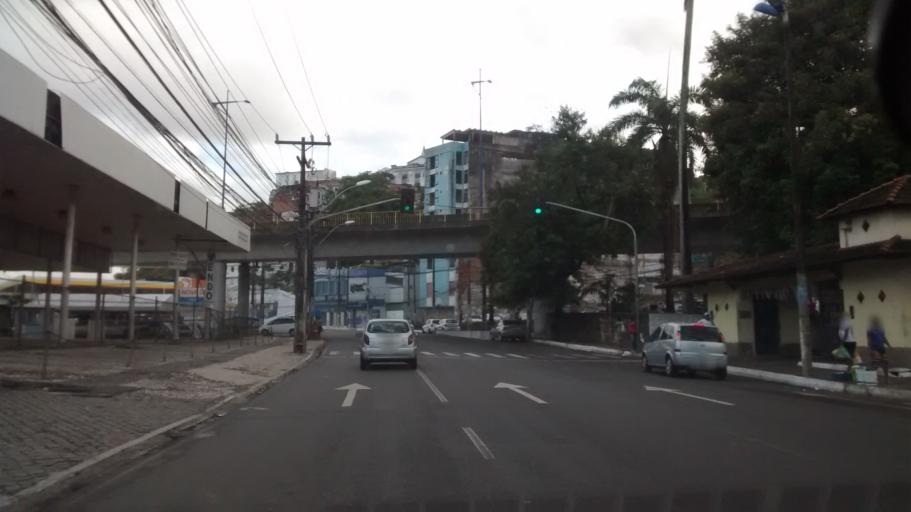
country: BR
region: Bahia
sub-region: Salvador
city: Salvador
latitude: -12.9586
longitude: -38.5025
